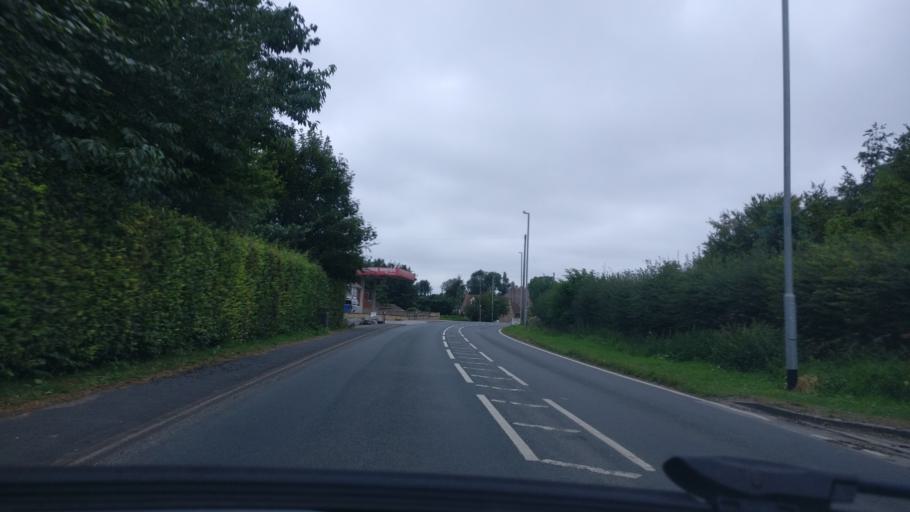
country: GB
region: England
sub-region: East Riding of Yorkshire
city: Leven
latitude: 53.8855
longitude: -0.3152
